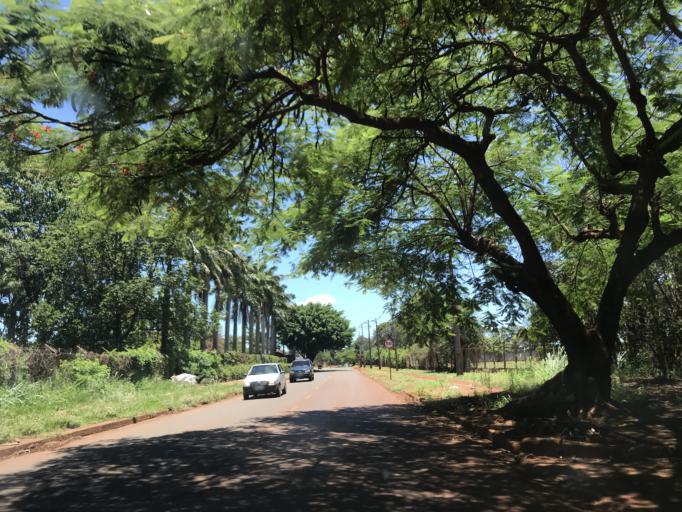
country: BR
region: Parana
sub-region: Sarandi
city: Sarandi
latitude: -23.4437
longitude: -51.9065
